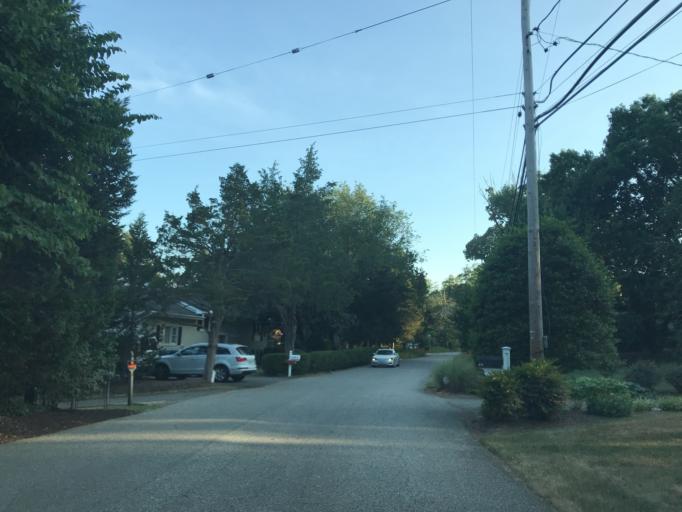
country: US
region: Maryland
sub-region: Anne Arundel County
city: Robinwood
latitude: 38.9495
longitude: -76.5284
